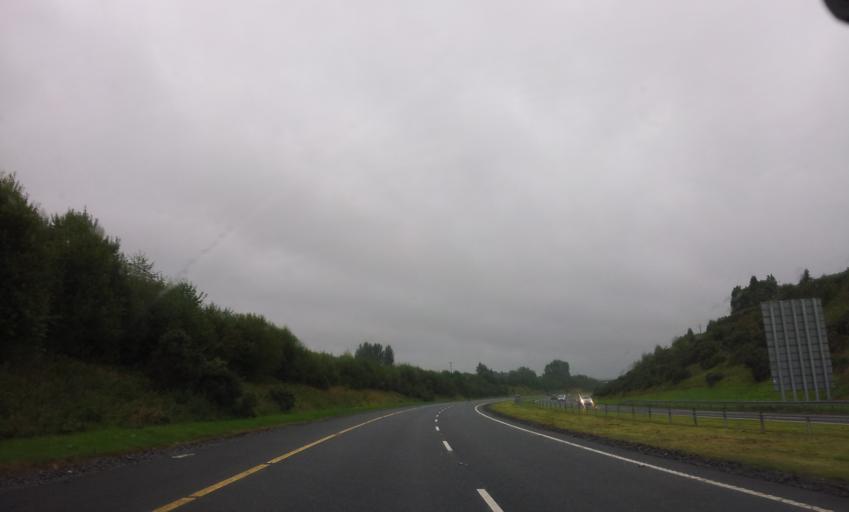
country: IE
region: Munster
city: Cahir
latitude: 52.3846
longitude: -7.9412
